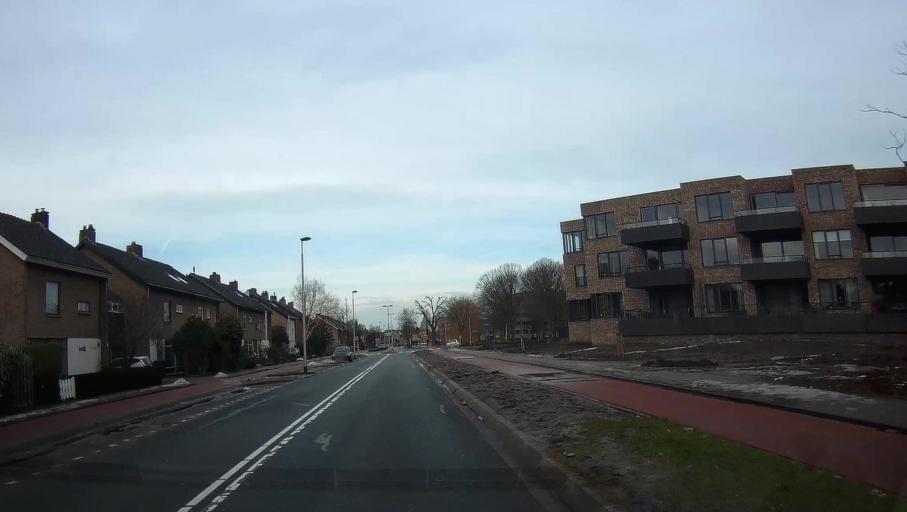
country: NL
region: South Holland
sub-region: Gemeente Barendrecht
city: Barendrecht
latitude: 51.8527
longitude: 4.5459
